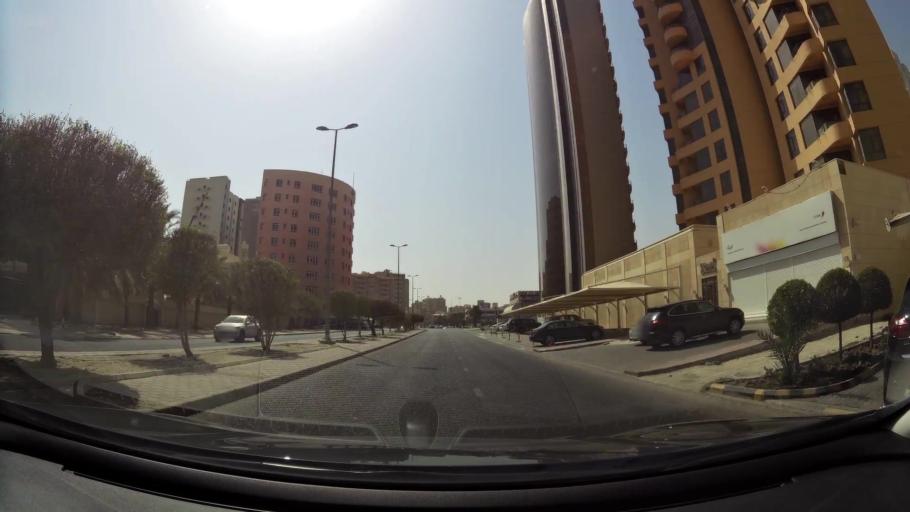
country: KW
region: Muhafazat Hawalli
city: Hawalli
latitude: 29.3400
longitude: 48.0483
